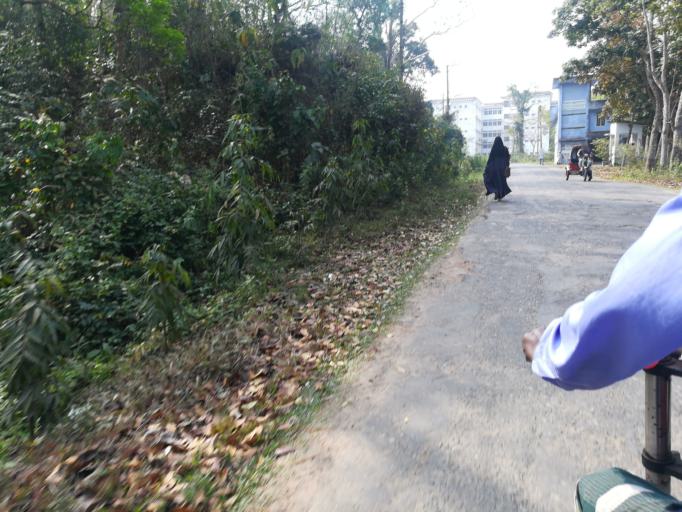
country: BD
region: Chittagong
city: Chittagong
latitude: 22.4693
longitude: 91.7809
